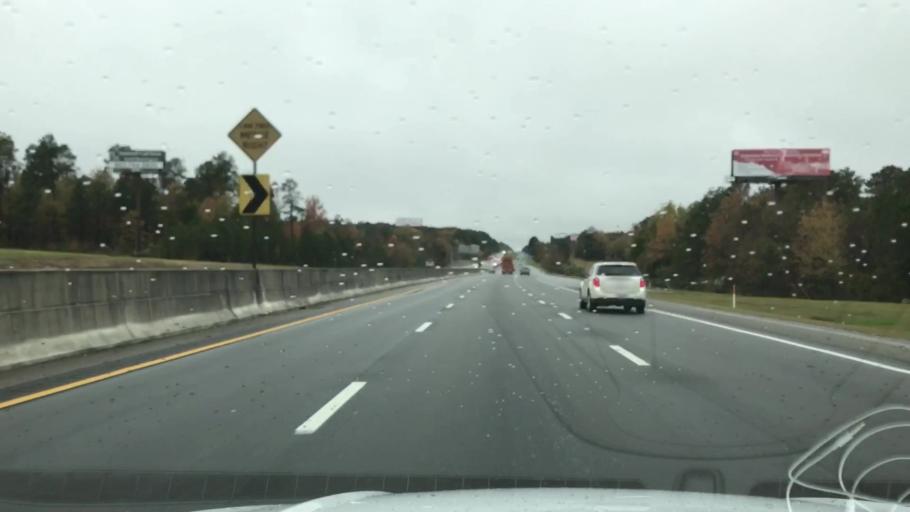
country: US
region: South Carolina
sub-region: Lexington County
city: Irmo
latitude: 34.1005
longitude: -81.1764
